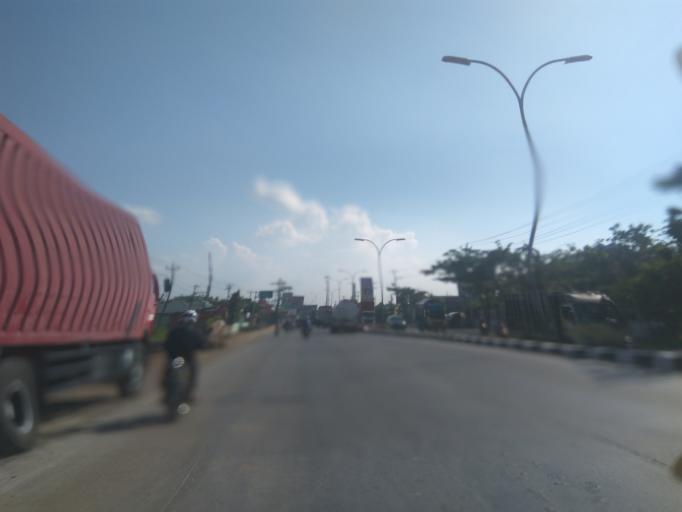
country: ID
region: Central Java
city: Semarang
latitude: -6.9507
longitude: 110.4829
